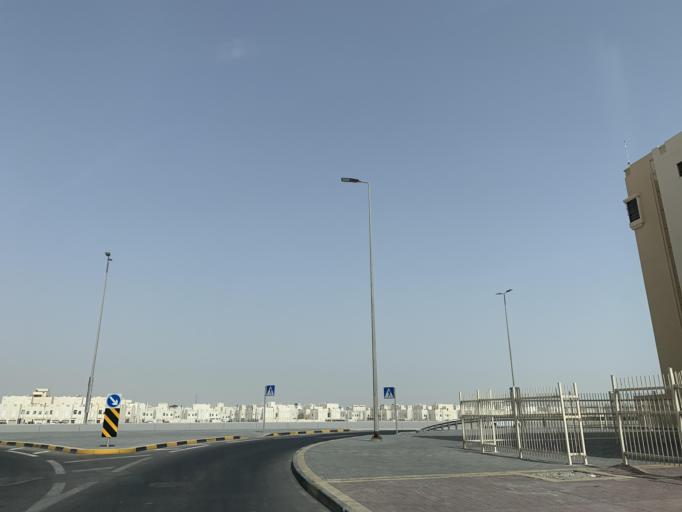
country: BH
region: Northern
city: Madinat `Isa
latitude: 26.1729
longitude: 50.5203
